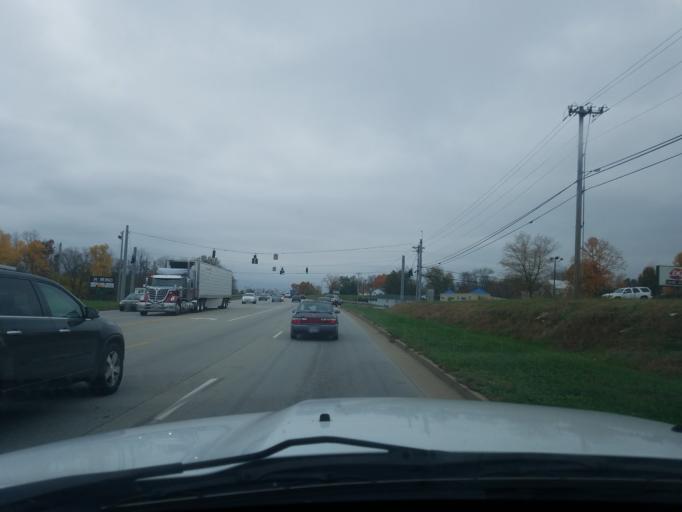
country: US
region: Kentucky
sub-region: Nelson County
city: Bardstown
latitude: 37.8251
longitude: -85.4559
